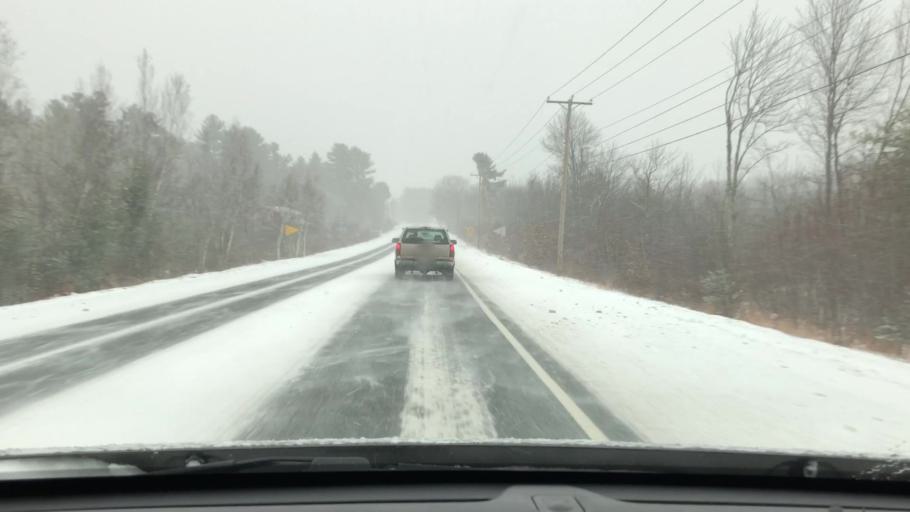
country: US
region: New Hampshire
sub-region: Strafford County
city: Lee
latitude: 43.1792
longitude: -71.0005
